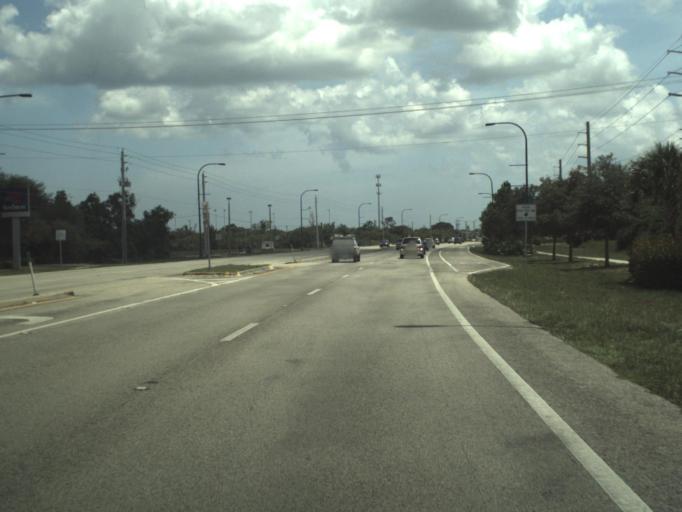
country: US
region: Florida
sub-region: Martin County
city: Hobe Sound
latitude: 27.0836
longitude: -80.1477
